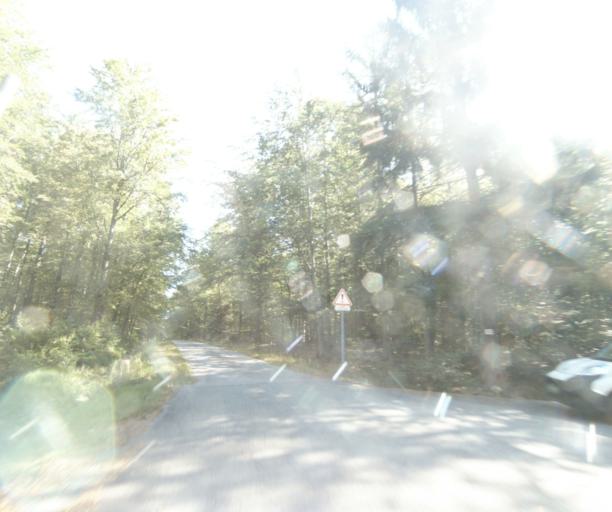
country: FR
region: Lorraine
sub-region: Departement des Vosges
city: Deyvillers
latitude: 48.1668
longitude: 6.5406
